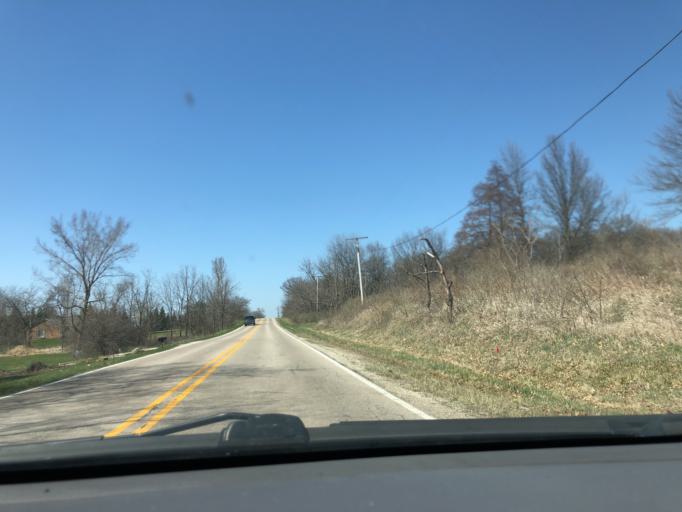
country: US
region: Illinois
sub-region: Kane County
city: Hampshire
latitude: 42.1088
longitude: -88.4912
